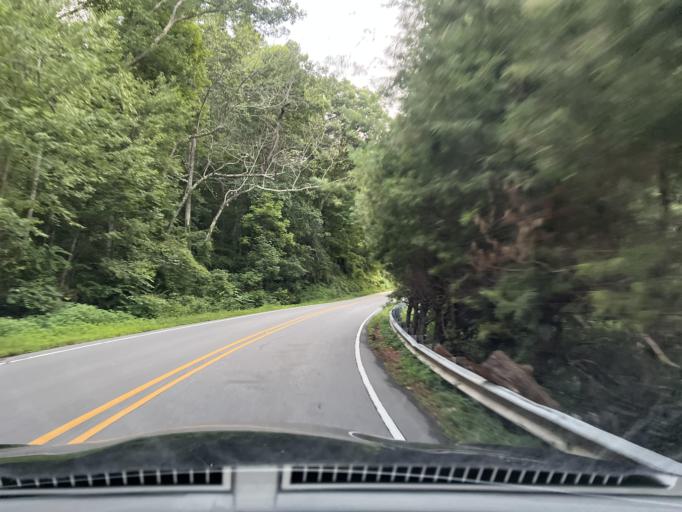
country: US
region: North Carolina
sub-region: Buncombe County
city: Asheville
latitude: 35.6228
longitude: -82.5302
